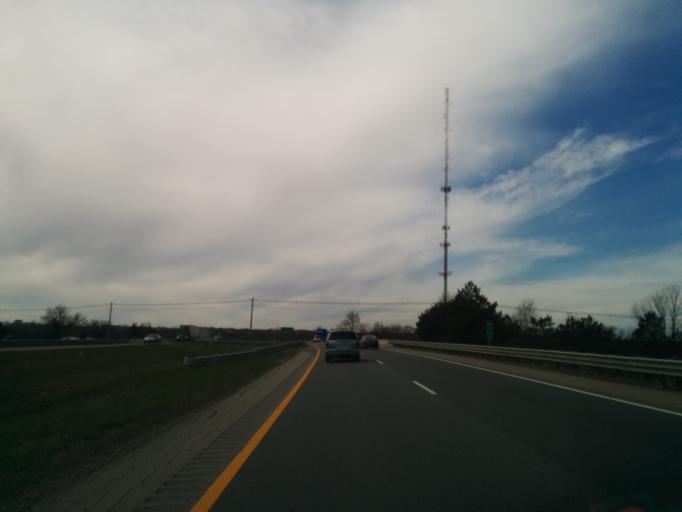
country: US
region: Michigan
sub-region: Ottawa County
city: Zeeland
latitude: 42.7926
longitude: -86.0171
